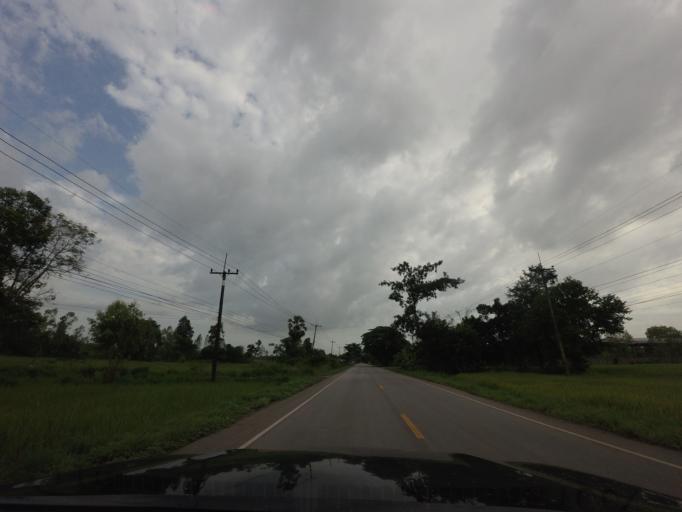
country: TH
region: Changwat Udon Thani
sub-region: Amphoe Ban Phue
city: Ban Phue
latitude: 17.7331
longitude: 102.3962
